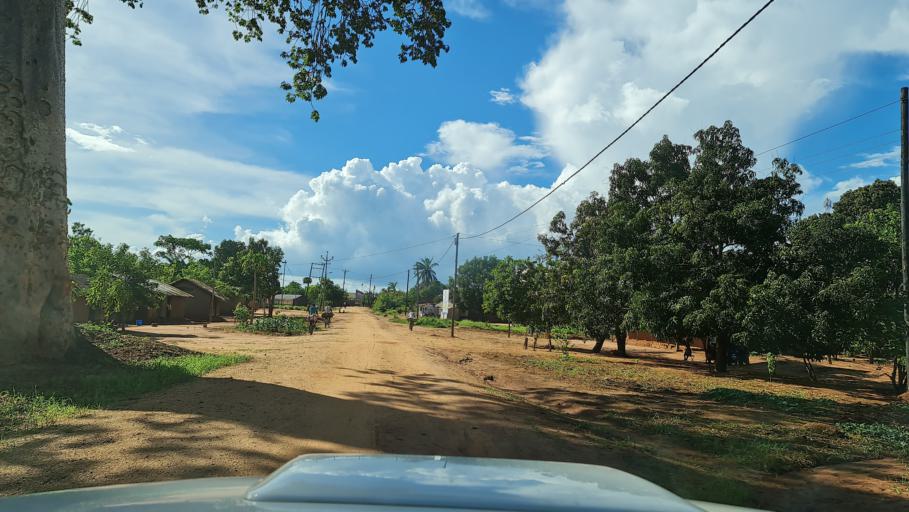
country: MZ
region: Nampula
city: Ilha de Mocambique
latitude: -15.2907
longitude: 40.1163
